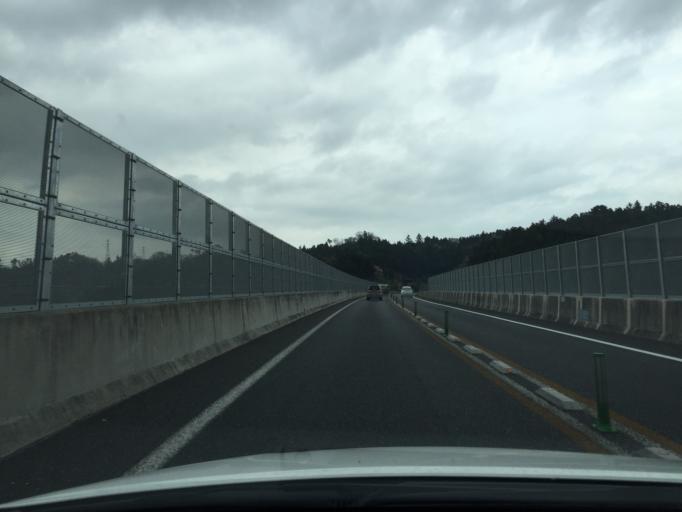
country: JP
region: Fukushima
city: Iwaki
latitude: 37.1692
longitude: 140.9680
